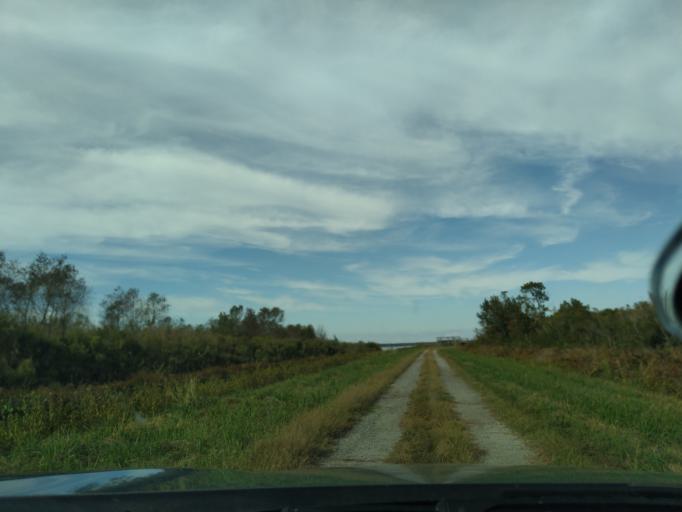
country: US
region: North Carolina
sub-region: Beaufort County
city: Belhaven
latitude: 35.6915
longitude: -76.5425
